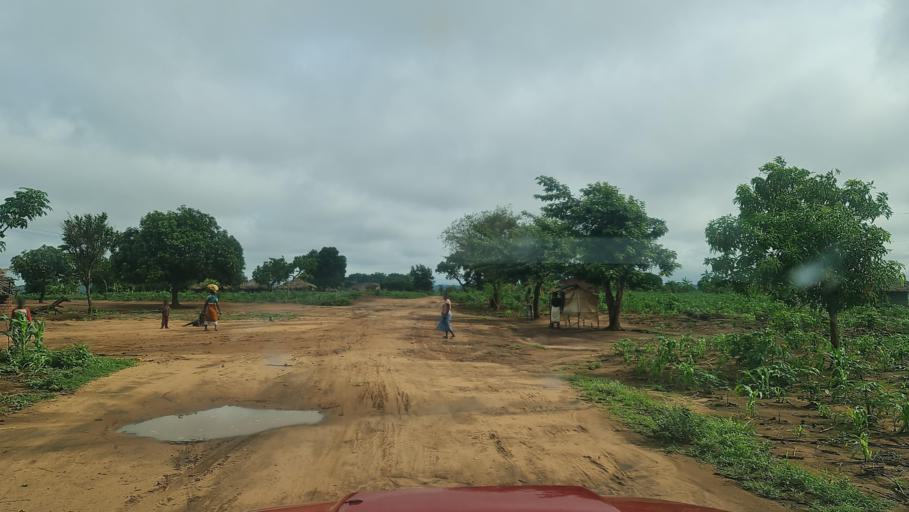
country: MW
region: Southern Region
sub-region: Nsanje District
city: Nsanje
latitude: -17.2134
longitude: 35.6769
